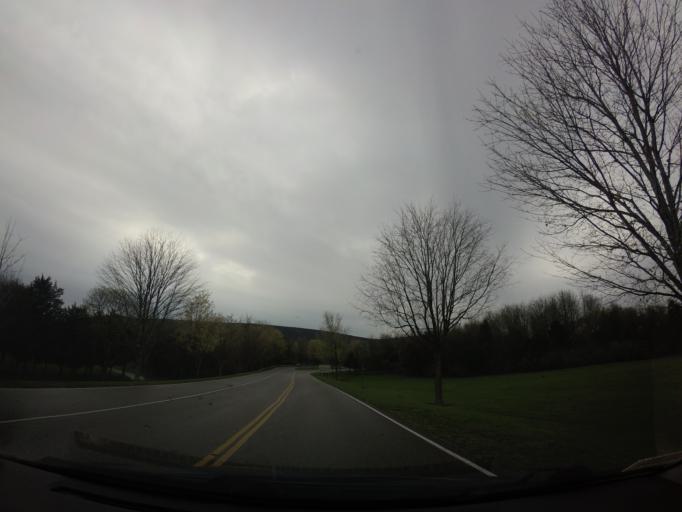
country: US
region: West Virginia
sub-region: Jefferson County
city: Bolivar
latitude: 39.3181
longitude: -77.7584
